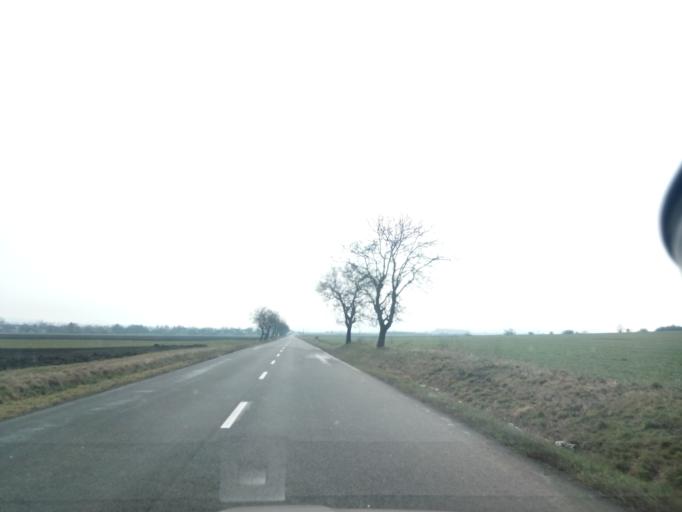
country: SK
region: Kosicky
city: Trebisov
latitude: 48.5754
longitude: 21.6420
